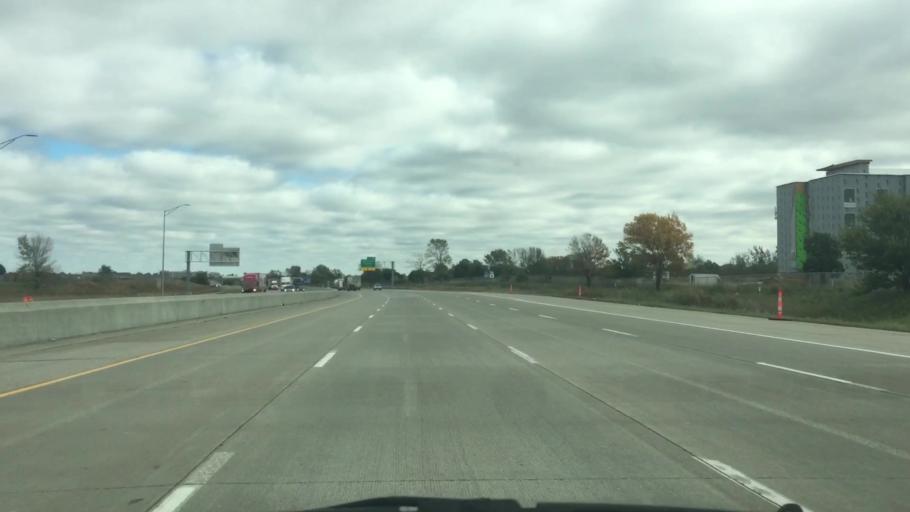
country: US
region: Iowa
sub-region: Polk County
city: Altoona
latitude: 41.6616
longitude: -93.4860
